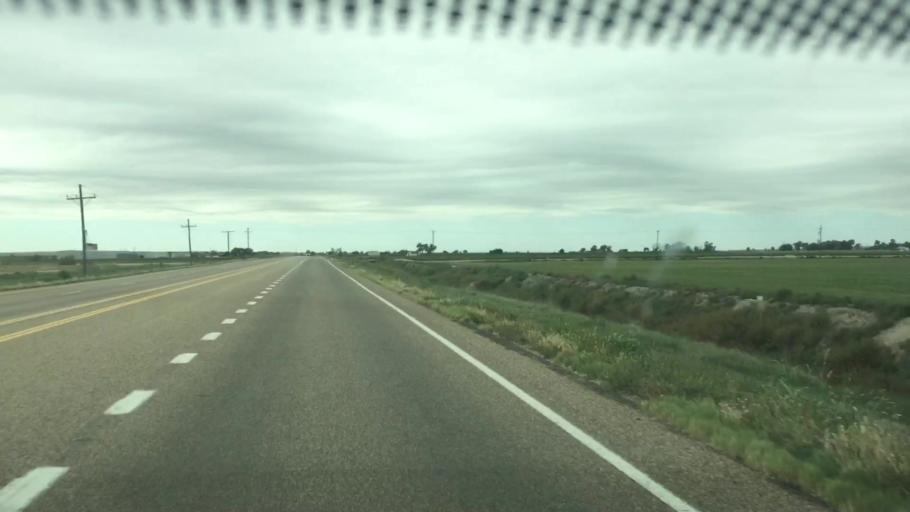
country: US
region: Colorado
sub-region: Prowers County
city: Lamar
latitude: 38.0574
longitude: -102.1894
